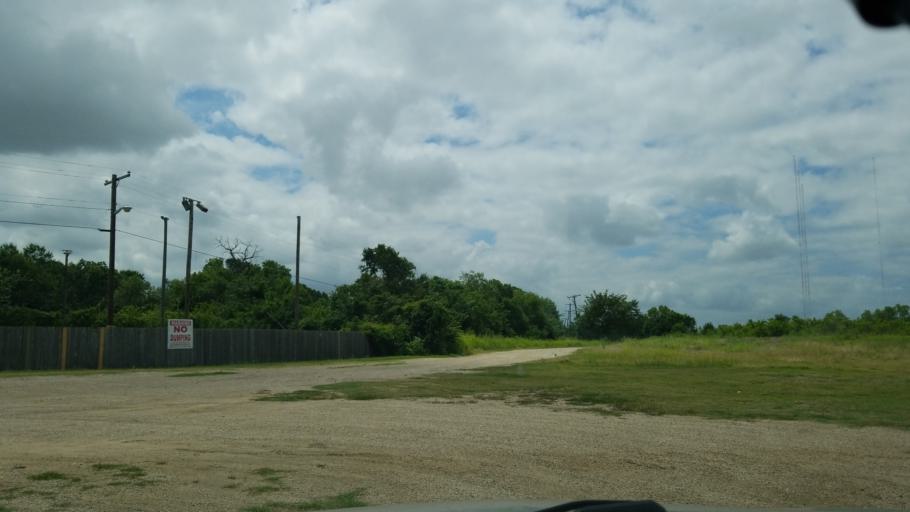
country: US
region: Texas
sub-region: Dallas County
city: Carrollton
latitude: 32.9506
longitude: -96.9404
